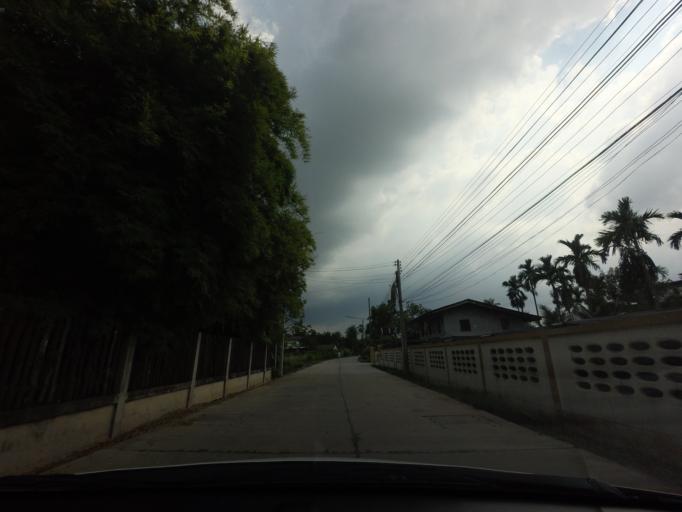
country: TH
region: Nakhon Pathom
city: Nakhon Chai Si
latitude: 13.7852
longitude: 100.2338
